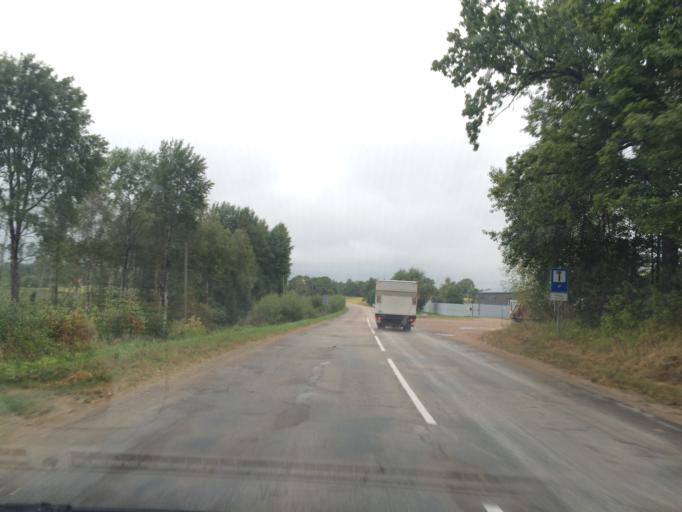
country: LV
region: Ikskile
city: Ikskile
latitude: 56.8552
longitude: 24.5308
